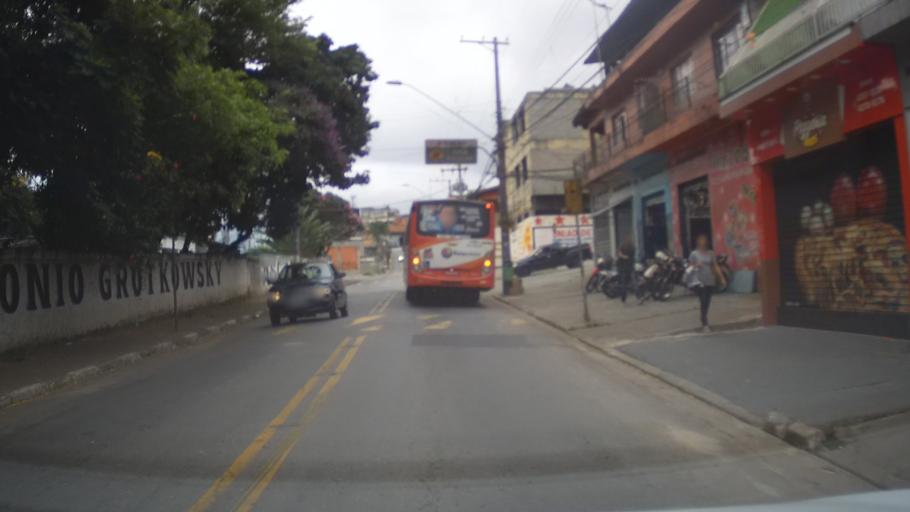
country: BR
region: Sao Paulo
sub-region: Guarulhos
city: Guarulhos
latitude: -23.4139
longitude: -46.4513
